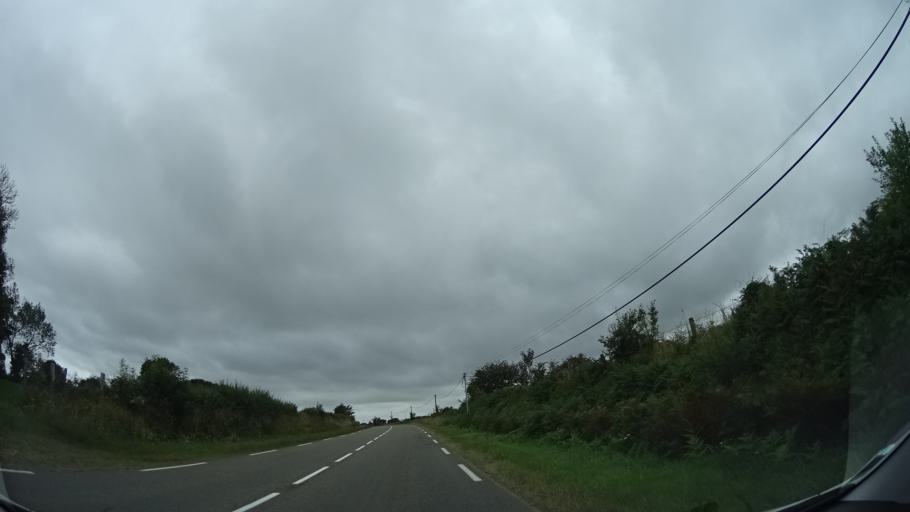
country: FR
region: Lower Normandy
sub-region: Departement de la Manche
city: La Haye-du-Puits
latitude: 49.3068
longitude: -1.5894
